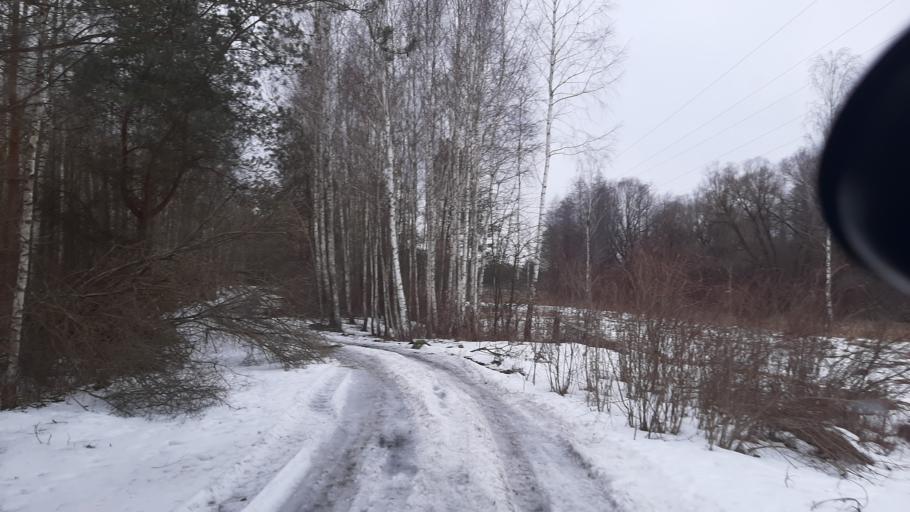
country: PL
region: Lublin Voivodeship
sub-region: Powiat wlodawski
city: Wlodawa
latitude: 51.5110
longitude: 23.6160
